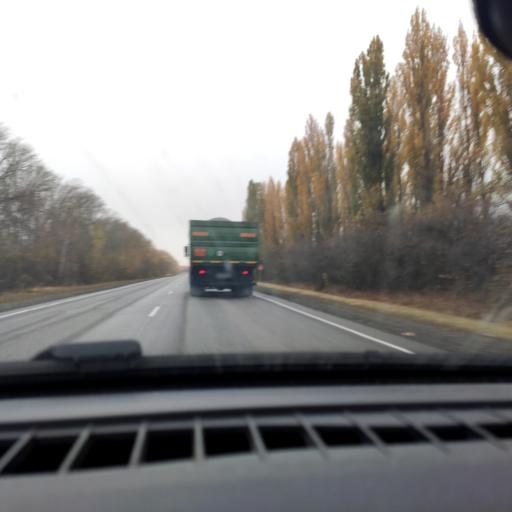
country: RU
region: Voronezj
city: Ostrogozhsk
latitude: 50.9642
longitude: 39.0165
